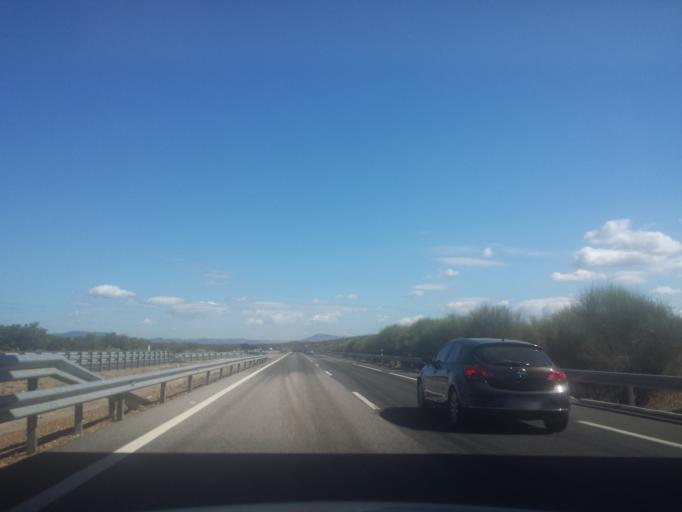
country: ES
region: Andalusia
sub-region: Provincia de Huelva
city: Santa Olalla del Cala
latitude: 37.8428
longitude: -6.2198
